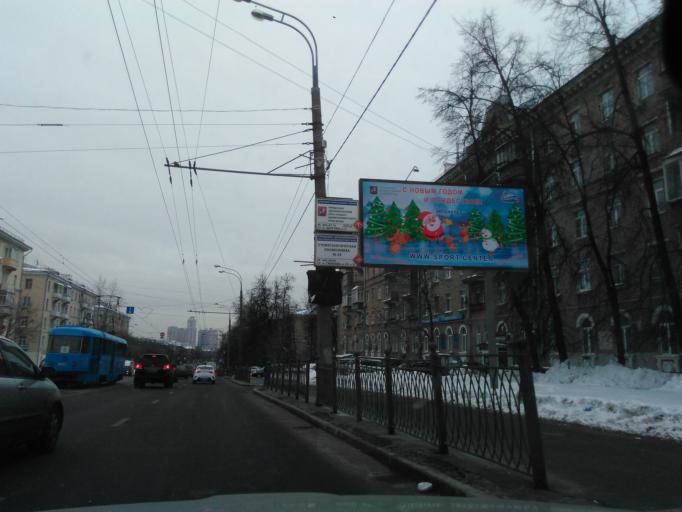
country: RU
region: Moscow
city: Pokrovskoye-Streshnevo
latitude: 55.8324
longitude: 37.4533
